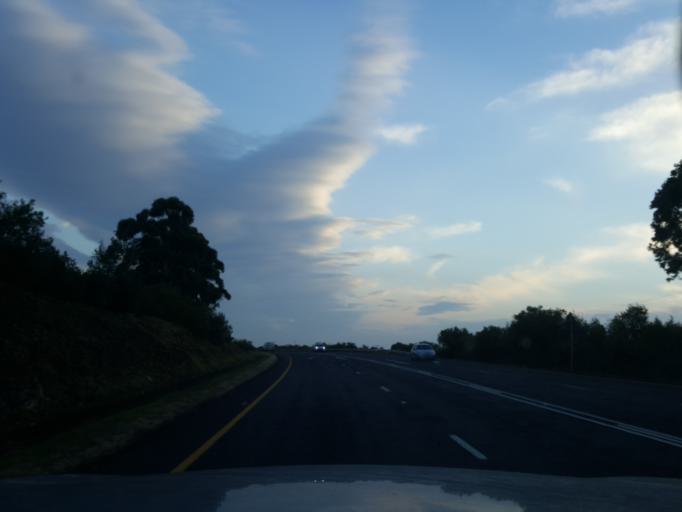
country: ZA
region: Eastern Cape
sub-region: Cacadu District Municipality
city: Grahamstown
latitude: -33.3781
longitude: 26.4497
